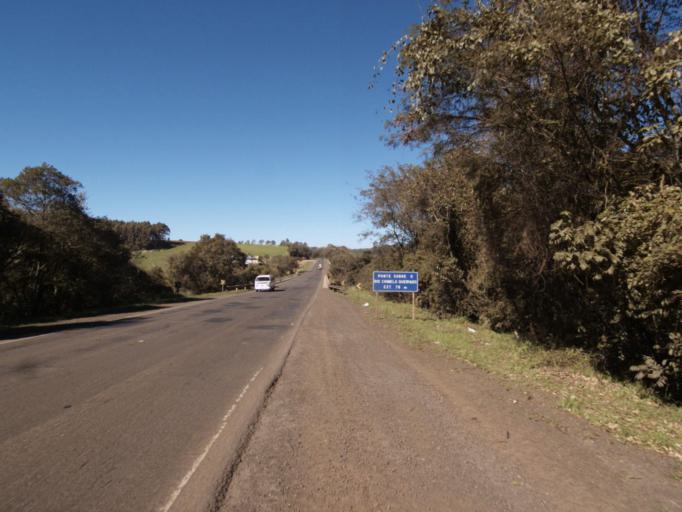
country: BR
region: Santa Catarina
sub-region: Sao Lourenco Do Oeste
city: Sao Lourenco dOeste
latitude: -26.7976
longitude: -53.1920
